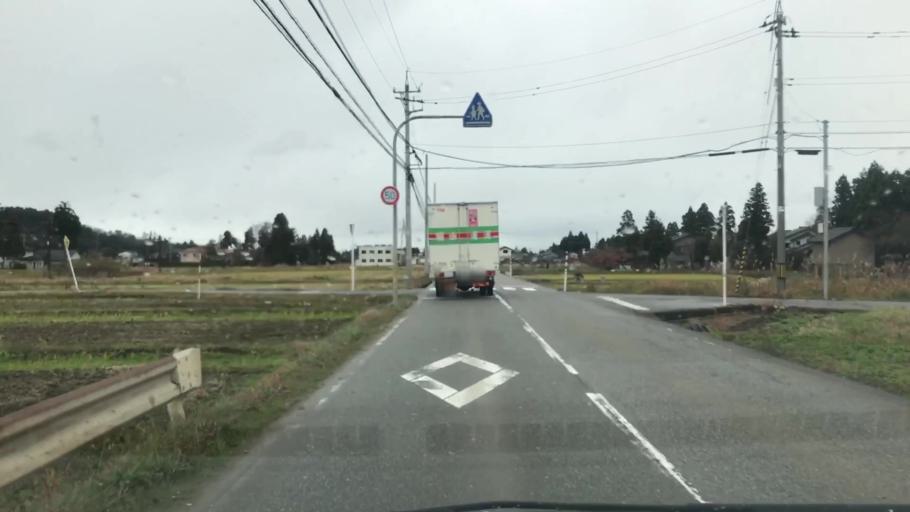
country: JP
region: Toyama
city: Kamiichi
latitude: 36.5956
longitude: 137.3259
